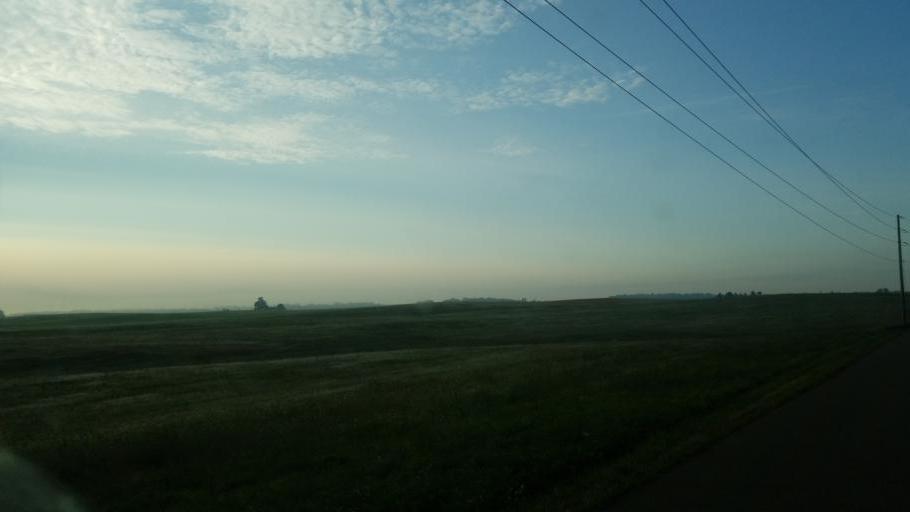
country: US
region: Ohio
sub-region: Knox County
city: Fredericktown
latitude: 40.4459
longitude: -82.6259
